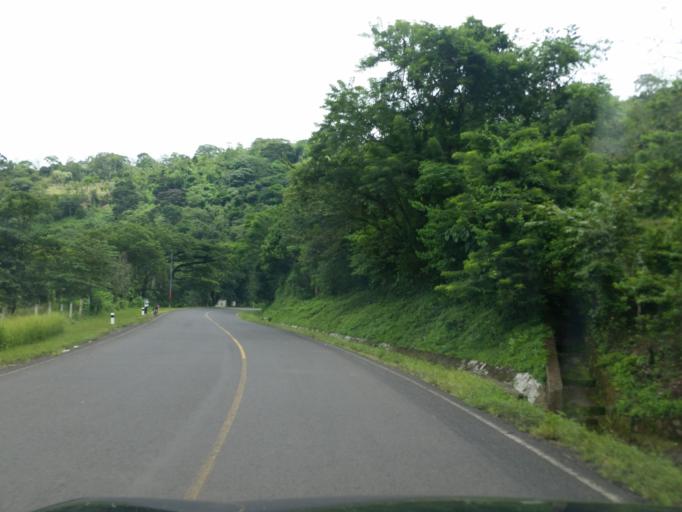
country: NI
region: Matagalpa
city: San Ramon
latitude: 13.0145
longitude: -85.7937
